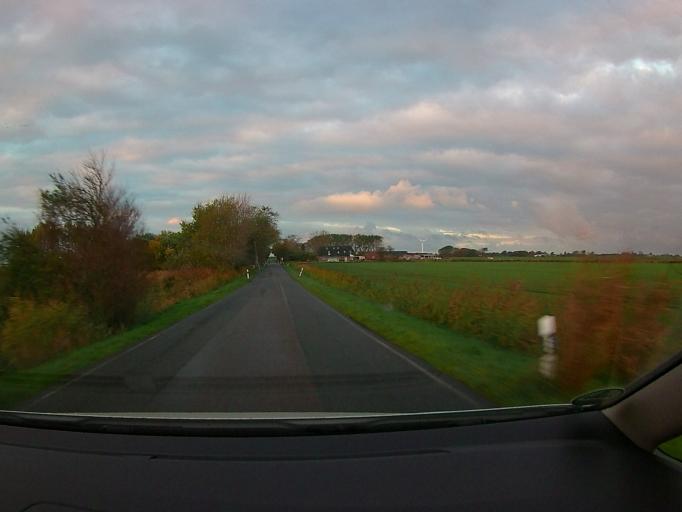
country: DE
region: Schleswig-Holstein
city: Galmsbull
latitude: 54.7180
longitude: 8.7553
